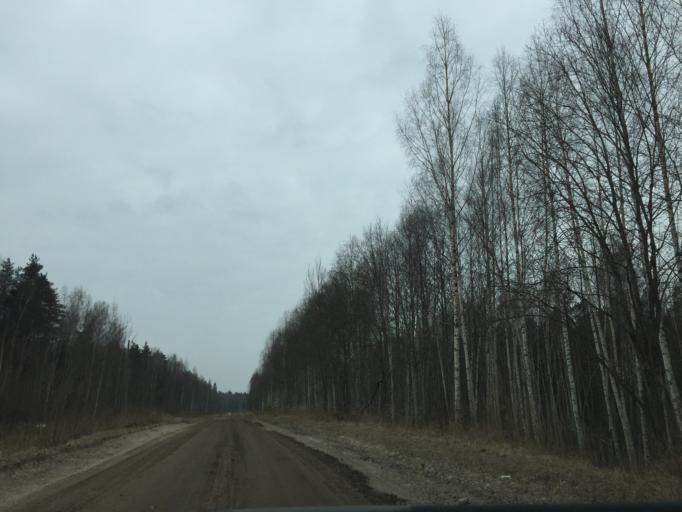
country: LV
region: Kekava
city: Balozi
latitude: 56.7874
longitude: 24.1301
